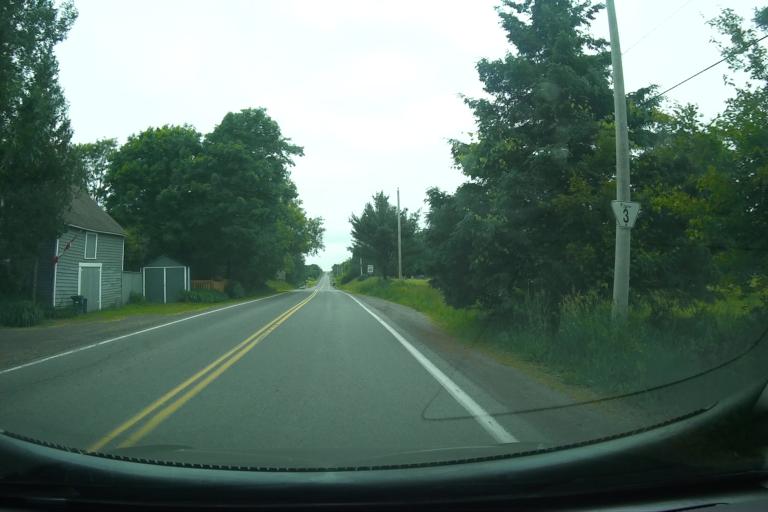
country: CA
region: Ontario
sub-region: Lanark County
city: Smiths Falls
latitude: 44.9847
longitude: -75.8009
